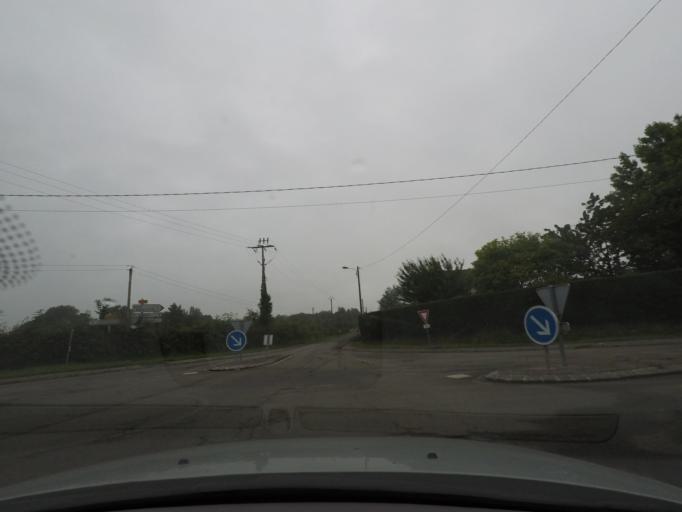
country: FR
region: Haute-Normandie
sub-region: Departement de la Seine-Maritime
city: Saint-Martin-Osmonville
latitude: 49.6088
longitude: 1.2455
